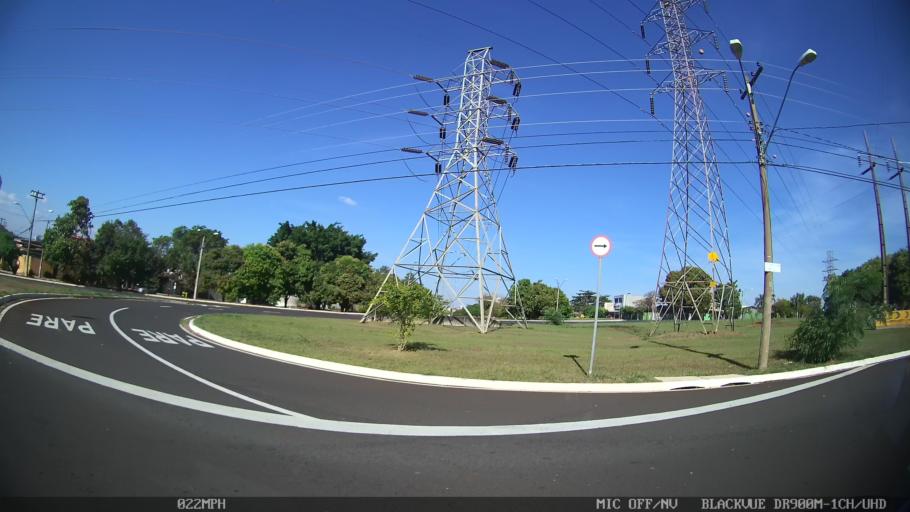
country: BR
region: Sao Paulo
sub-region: Ribeirao Preto
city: Ribeirao Preto
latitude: -21.1849
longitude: -47.7834
